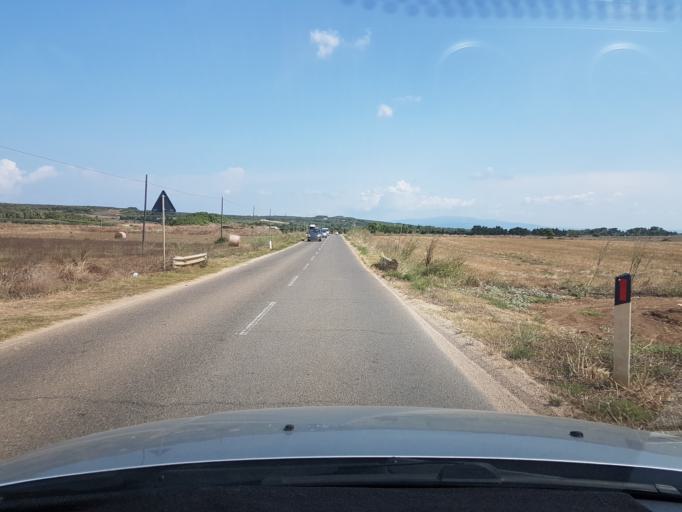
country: IT
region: Sardinia
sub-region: Provincia di Oristano
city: Cabras
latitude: 39.9077
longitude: 8.4383
